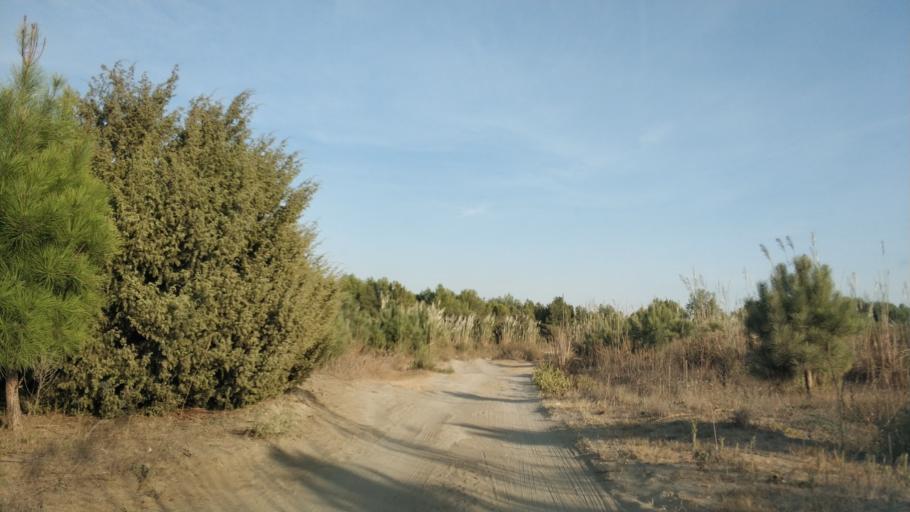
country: AL
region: Fier
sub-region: Rrethi i Lushnjes
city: Divjake
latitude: 40.9545
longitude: 19.4718
